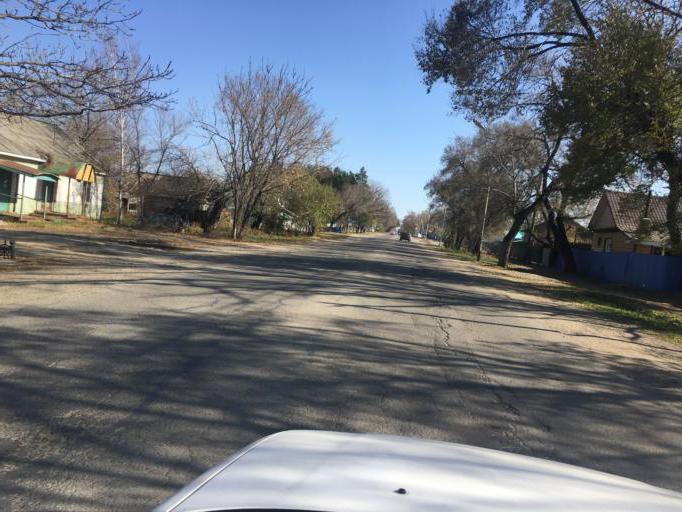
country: RU
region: Primorskiy
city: Dal'nerechensk
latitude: 45.9258
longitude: 133.7387
